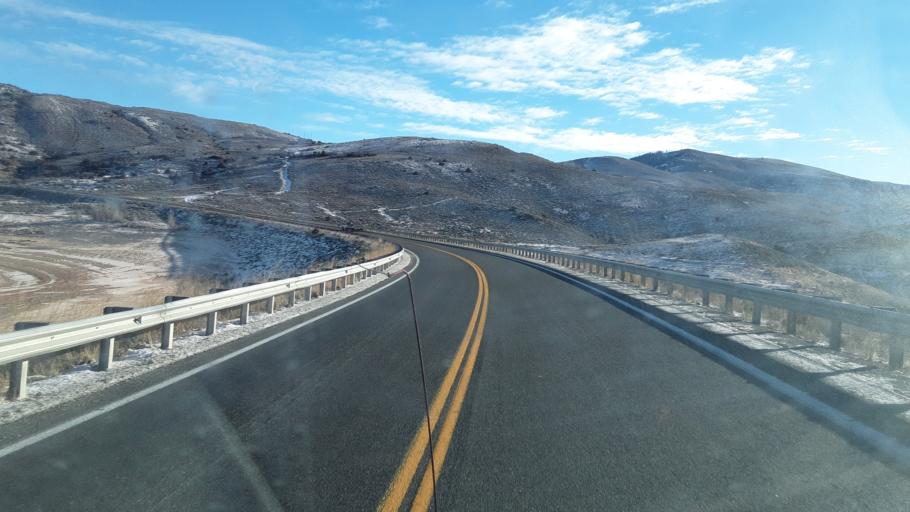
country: US
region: Colorado
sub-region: Gunnison County
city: Gunnison
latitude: 38.4507
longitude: -107.3041
